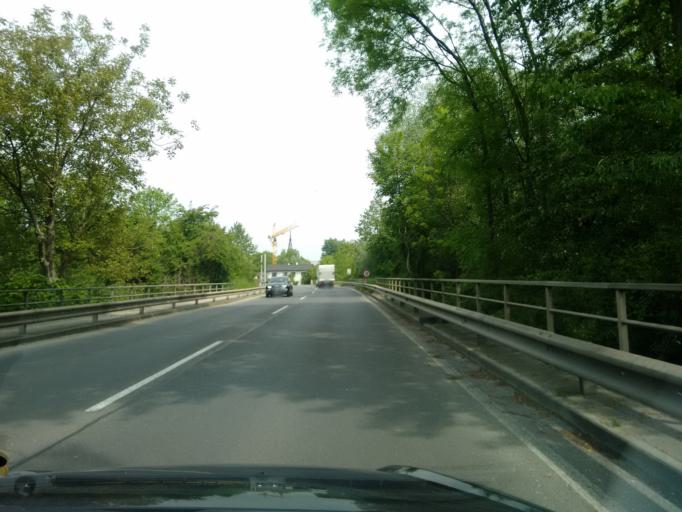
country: AT
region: Upper Austria
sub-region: Politischer Bezirk Linz-Land
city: Traun
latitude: 48.2161
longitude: 14.2402
